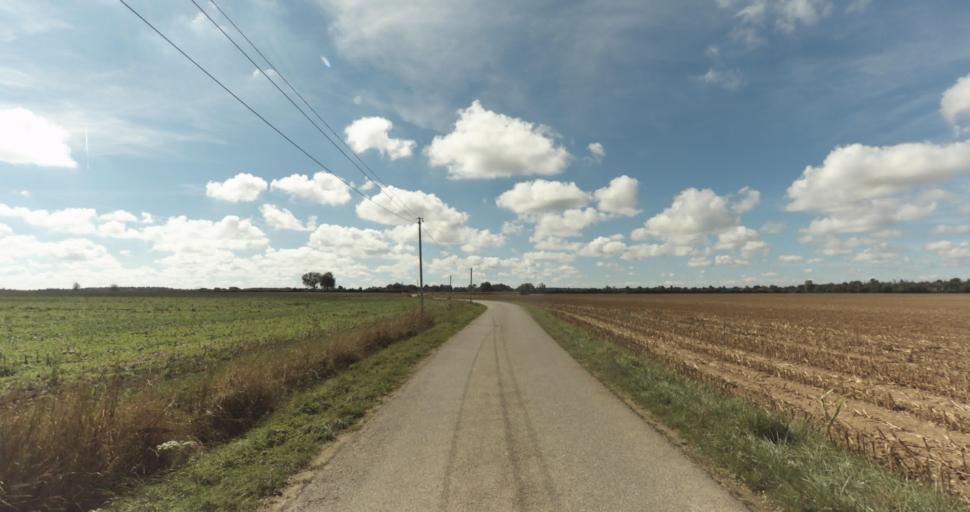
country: FR
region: Lower Normandy
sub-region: Departement du Calvados
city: Orbec
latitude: 48.9528
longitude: 0.4001
